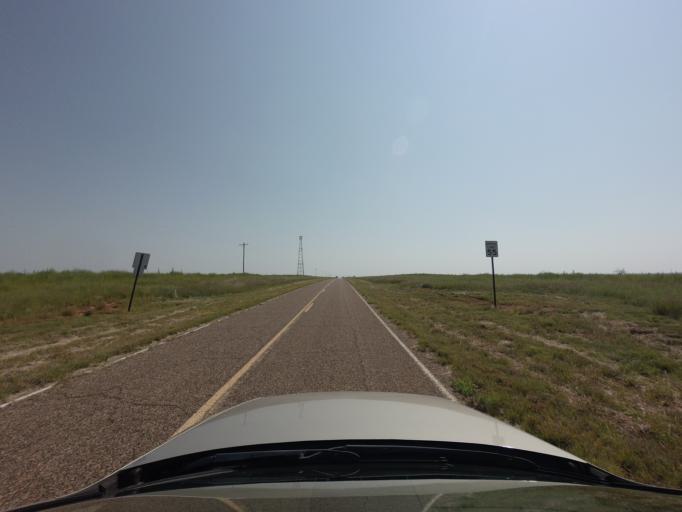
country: US
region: New Mexico
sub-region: Curry County
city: Cannon Air Force Base
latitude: 34.6336
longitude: -103.5644
